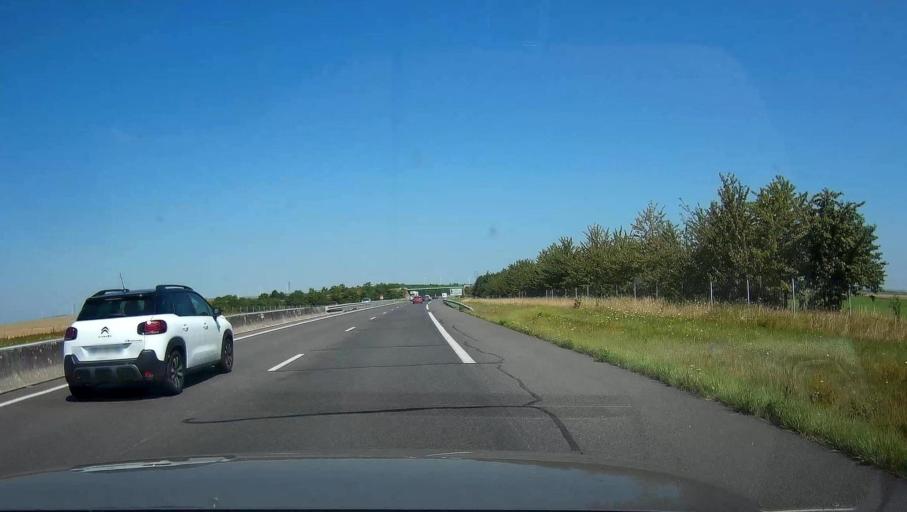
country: FR
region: Champagne-Ardenne
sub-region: Departement de l'Aube
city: Arcis-sur-Aube
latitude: 48.5034
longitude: 4.1664
